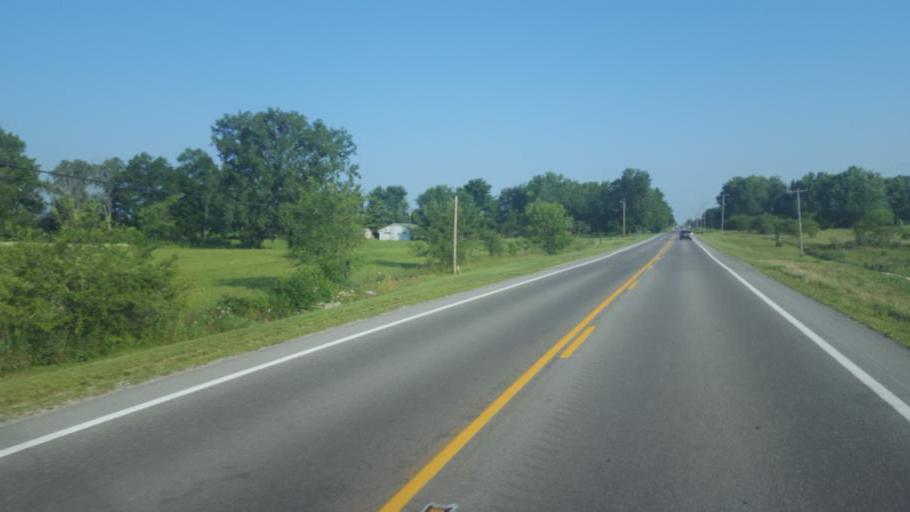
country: US
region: Ohio
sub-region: Hardin County
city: Kenton
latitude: 40.5816
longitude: -83.5595
